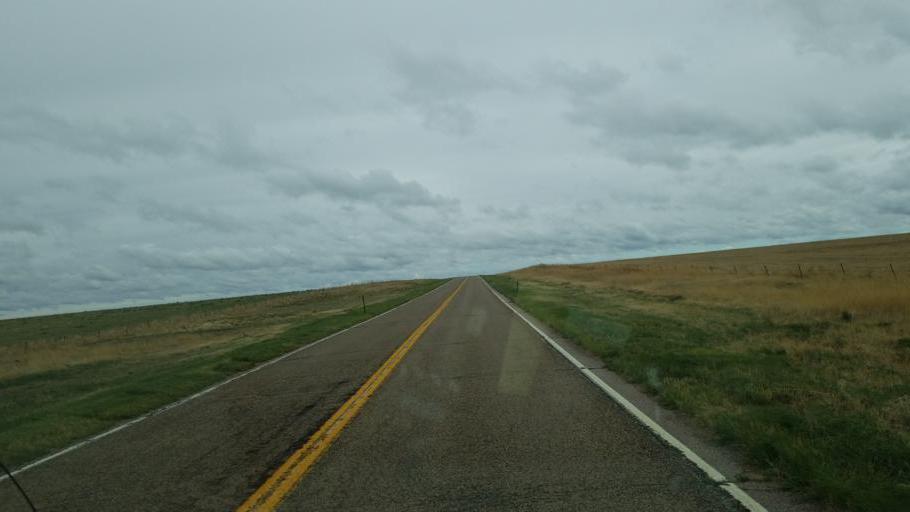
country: US
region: Colorado
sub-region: Lincoln County
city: Hugo
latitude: 38.8503
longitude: -103.4549
